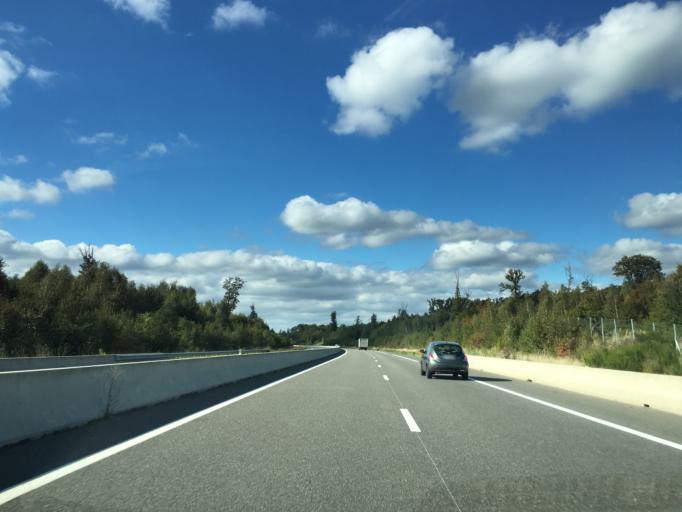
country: FR
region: Lorraine
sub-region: Departement de Meurthe-et-Moselle
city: Baccarat
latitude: 48.5077
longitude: 6.6714
